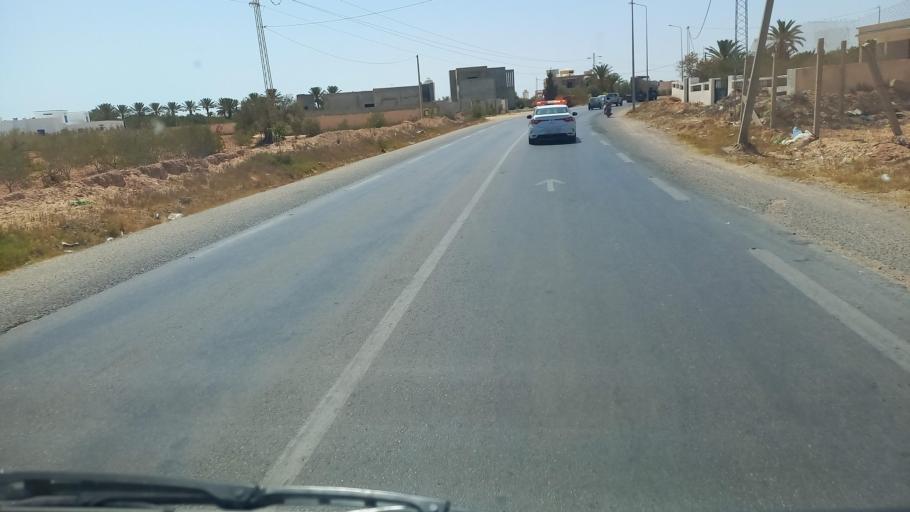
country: TN
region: Madanin
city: Houmt Souk
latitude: 33.7875
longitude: 10.8885
